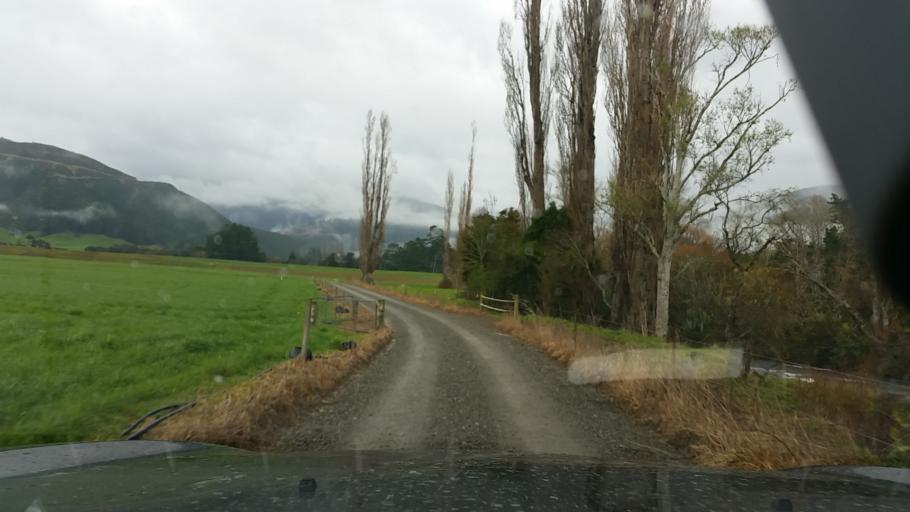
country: NZ
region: Nelson
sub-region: Nelson City
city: Nelson
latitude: -41.2683
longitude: 173.5756
